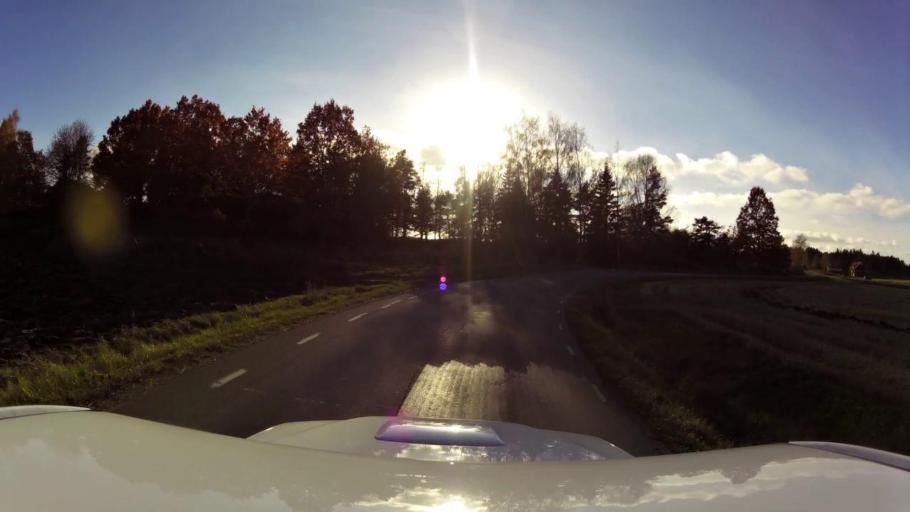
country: SE
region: OEstergoetland
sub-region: Linkopings Kommun
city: Vikingstad
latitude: 58.2845
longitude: 15.4393
